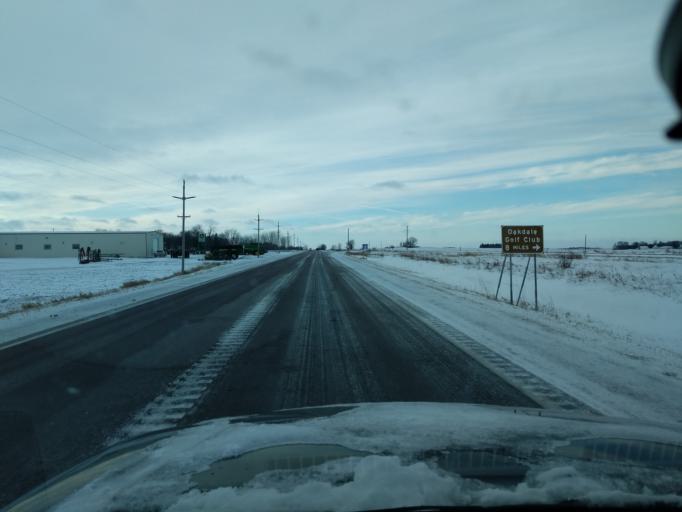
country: US
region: Minnesota
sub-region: Renville County
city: Hector
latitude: 44.7238
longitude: -94.5150
